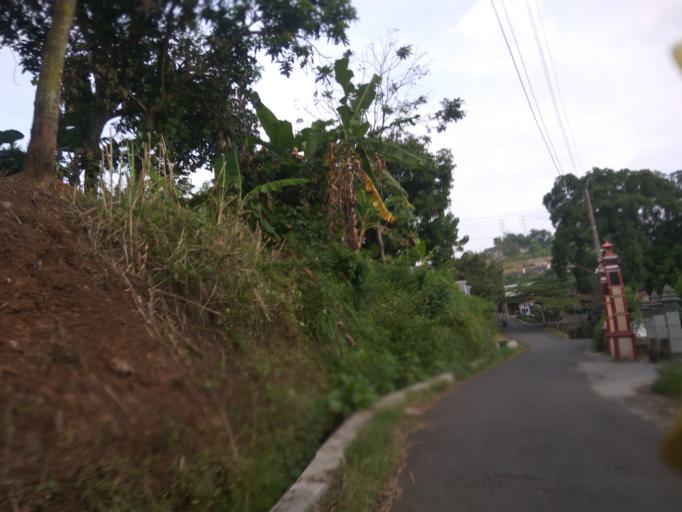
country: ID
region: Central Java
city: Semarang
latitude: -7.0219
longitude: 110.4418
